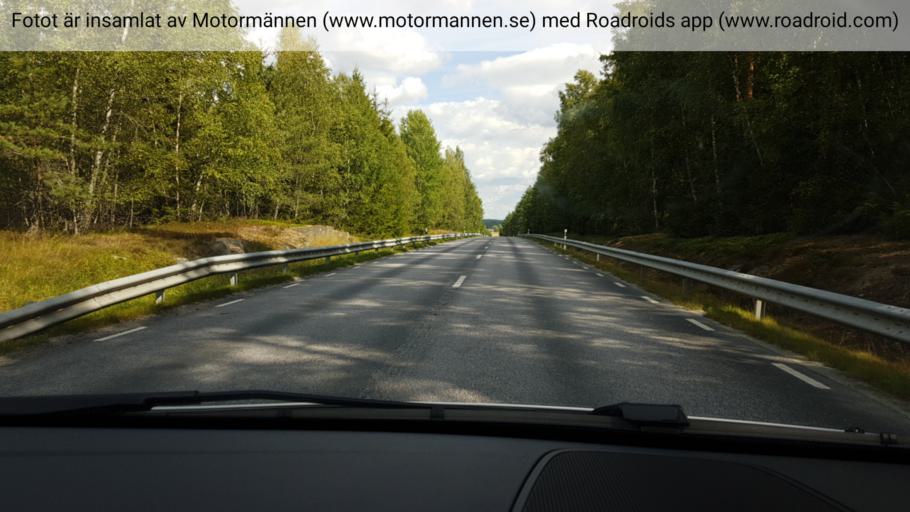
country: SE
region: Stockholm
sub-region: Vallentuna Kommun
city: Vallentuna
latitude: 59.7071
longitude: 18.0474
